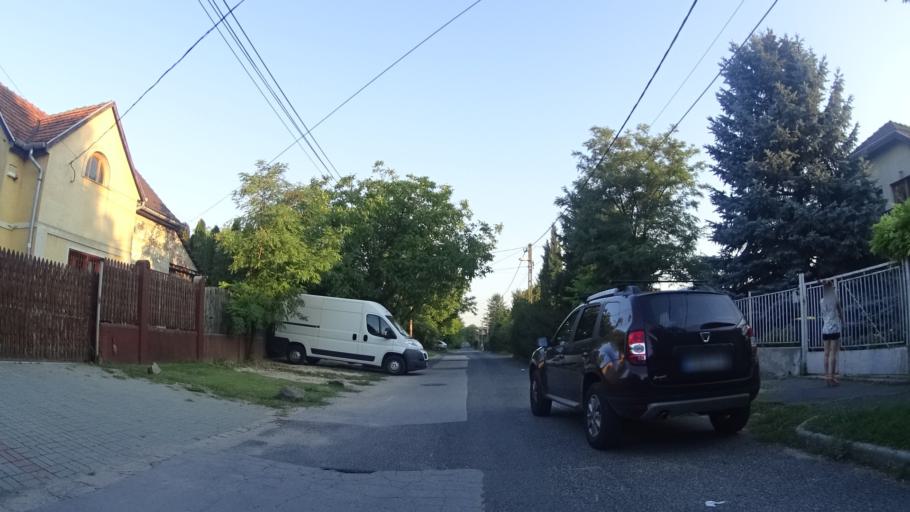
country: HU
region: Pest
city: Halasztelek
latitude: 47.3936
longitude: 19.0065
